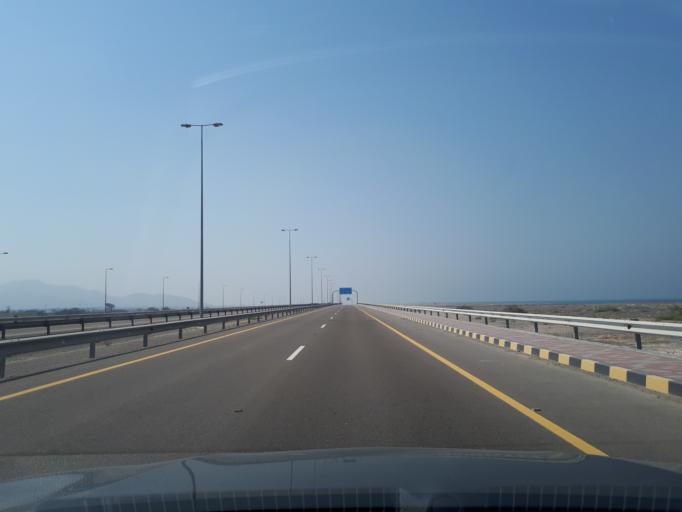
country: AE
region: Al Fujayrah
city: Al Fujayrah
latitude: 24.9410
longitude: 56.3822
